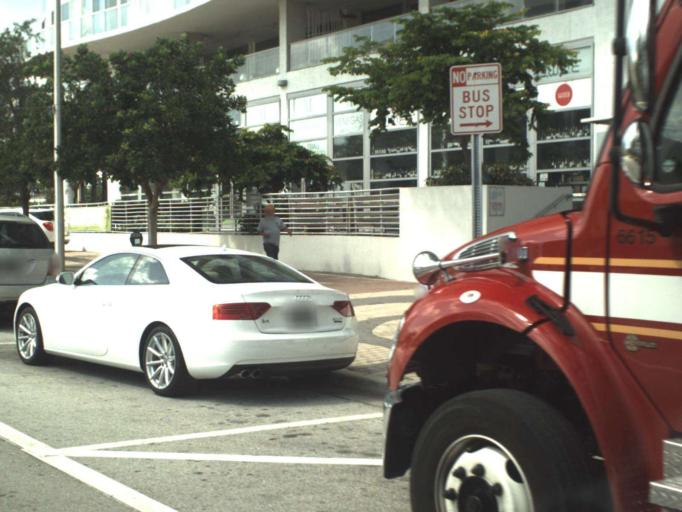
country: US
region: Florida
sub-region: Miami-Dade County
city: Miami
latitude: 25.7826
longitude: -80.1896
